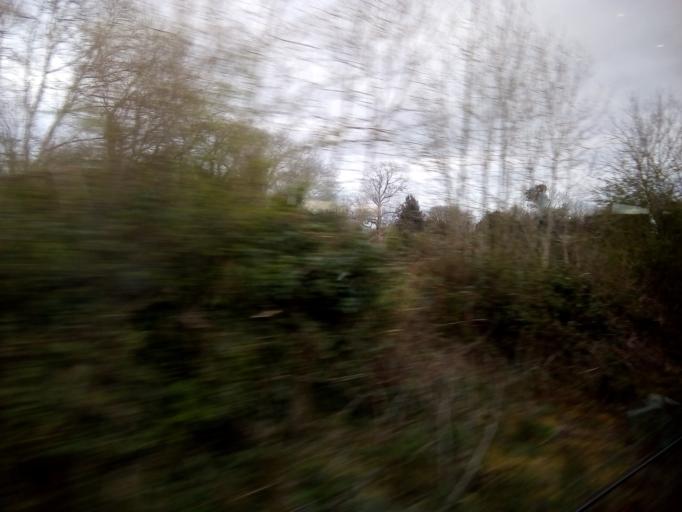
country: IE
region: Leinster
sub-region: An Longfort
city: Longford
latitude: 53.7587
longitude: -7.8277
